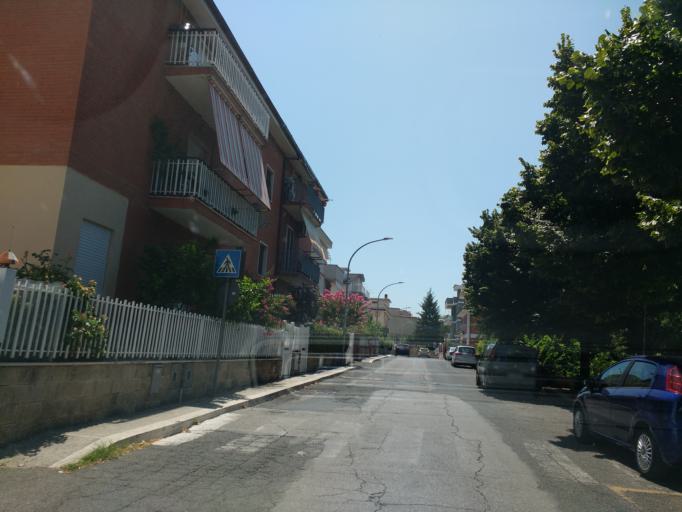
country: IT
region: Latium
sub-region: Citta metropolitana di Roma Capitale
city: Villa Adriana
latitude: 41.9525
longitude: 12.7720
